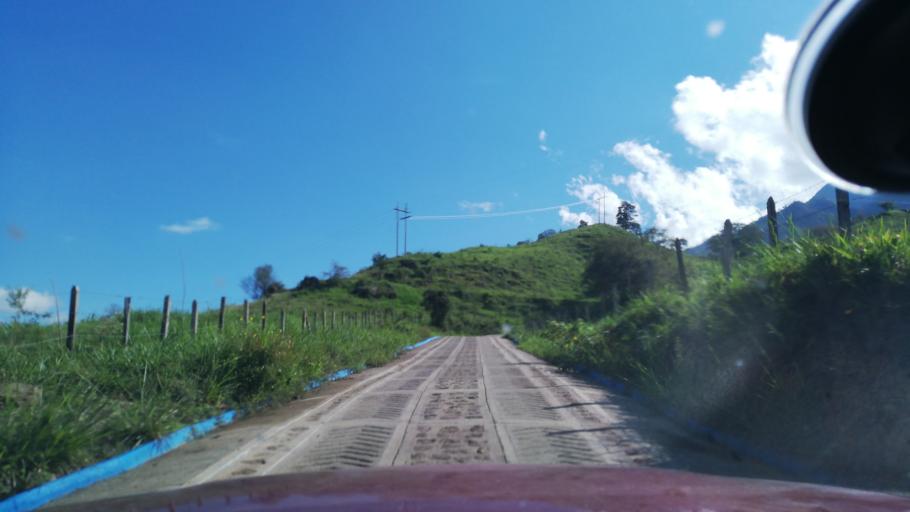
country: CO
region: Cundinamarca
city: Quipile
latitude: 4.7750
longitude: -74.6159
